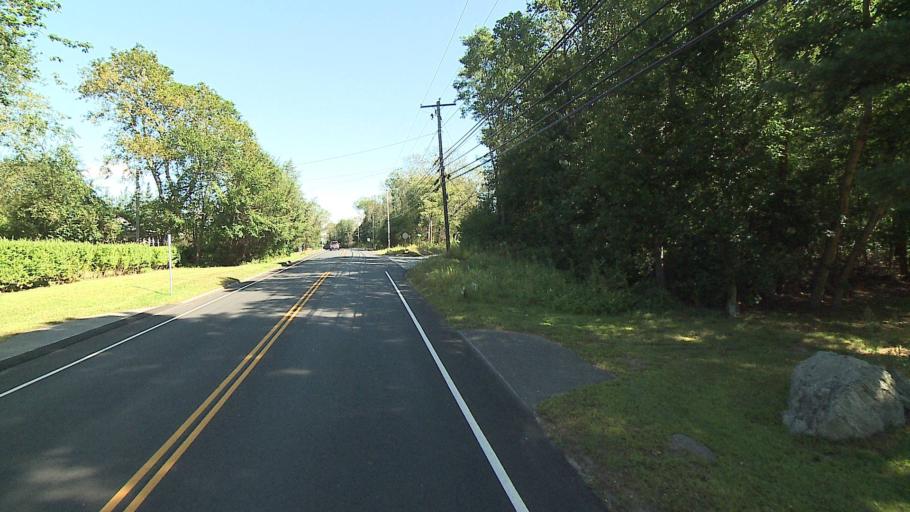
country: US
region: Connecticut
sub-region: Windham County
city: Wauregan
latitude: 41.7539
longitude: -71.9012
